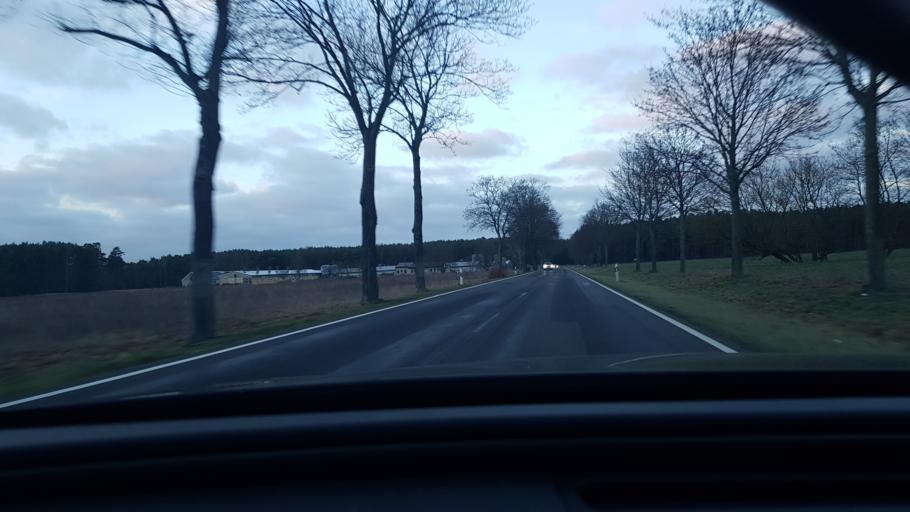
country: DE
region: Brandenburg
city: Storkow
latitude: 52.2922
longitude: 13.9049
